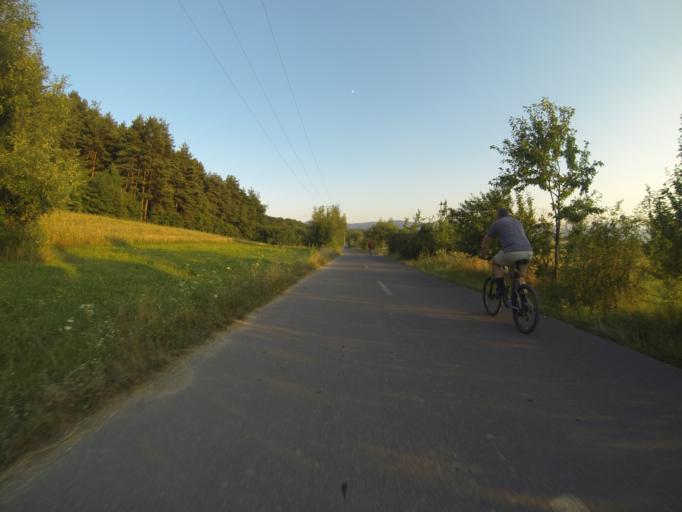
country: RO
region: Brasov
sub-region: Comuna Sinca Veche
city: Sinca Veche
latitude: 45.7577
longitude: 25.1646
